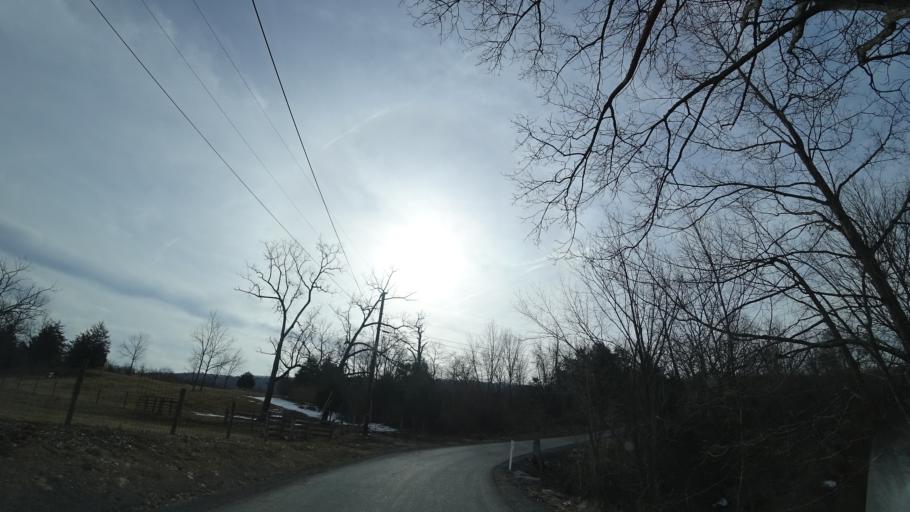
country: US
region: Virginia
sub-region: Shenandoah County
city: Woodstock
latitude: 39.0629
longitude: -78.6277
